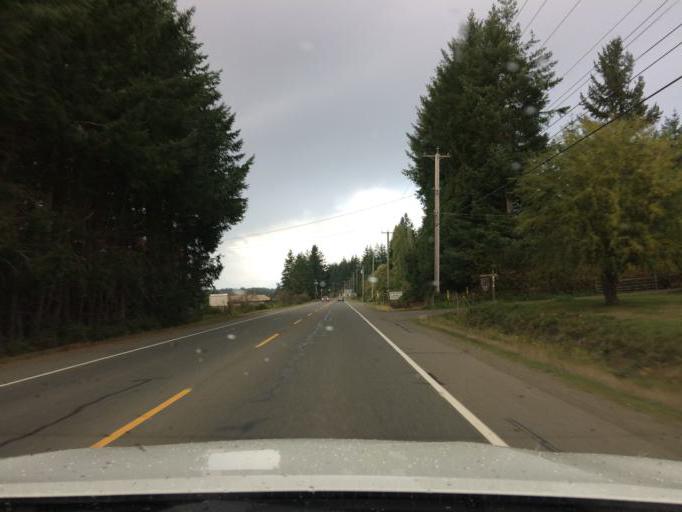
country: CA
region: British Columbia
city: Courtenay
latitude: 49.7638
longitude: -125.0227
